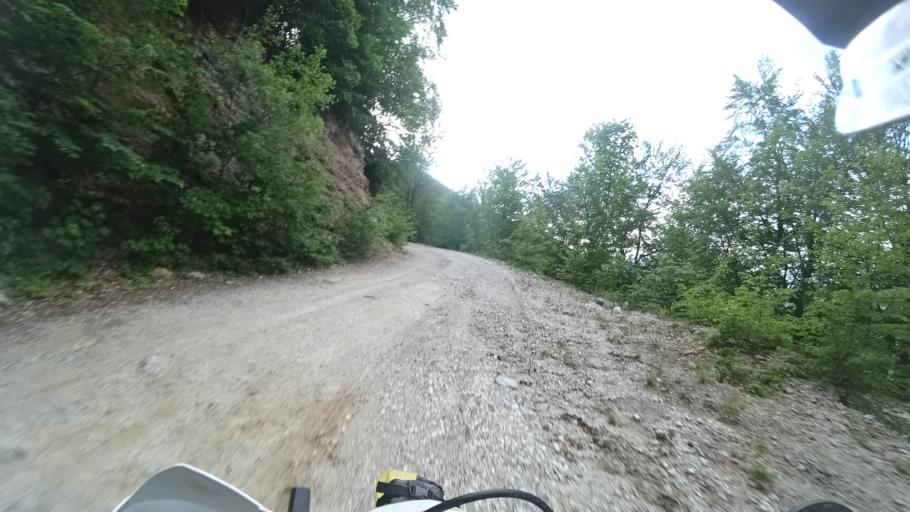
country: HR
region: Licko-Senjska
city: Gospic
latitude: 44.4681
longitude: 15.3157
